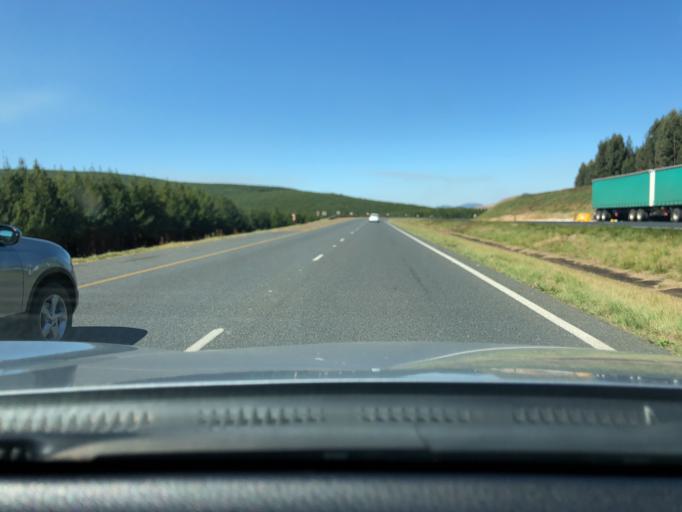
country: ZA
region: KwaZulu-Natal
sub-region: uMgungundlovu District Municipality
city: Howick
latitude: -29.3860
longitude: 30.1321
